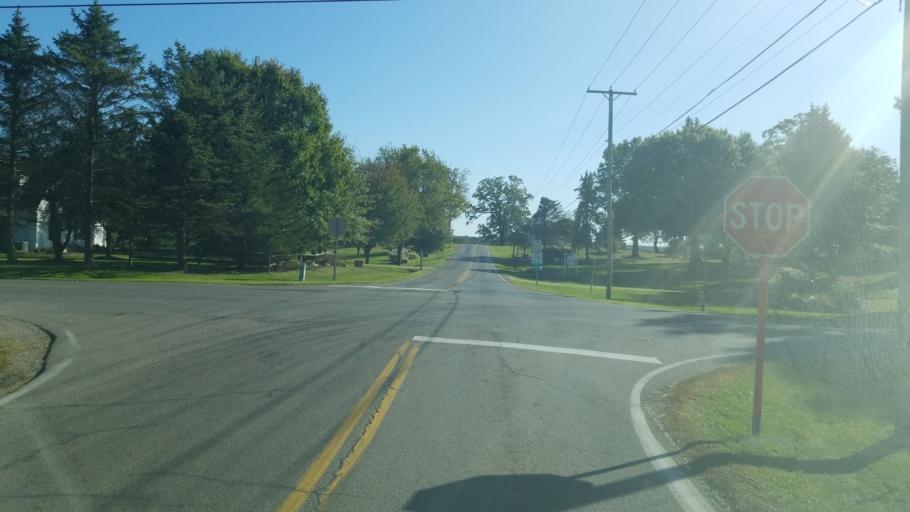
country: US
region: Ohio
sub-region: Medina County
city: Westfield Center
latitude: 41.0121
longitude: -81.9109
